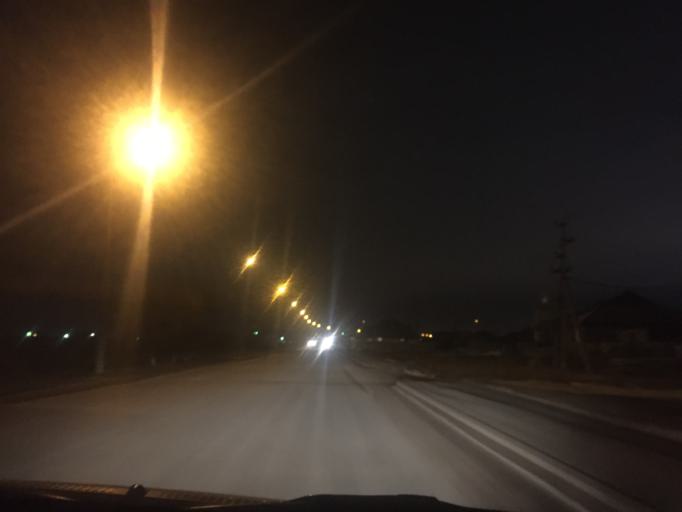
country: KZ
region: Astana Qalasy
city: Astana
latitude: 51.2157
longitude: 71.3946
